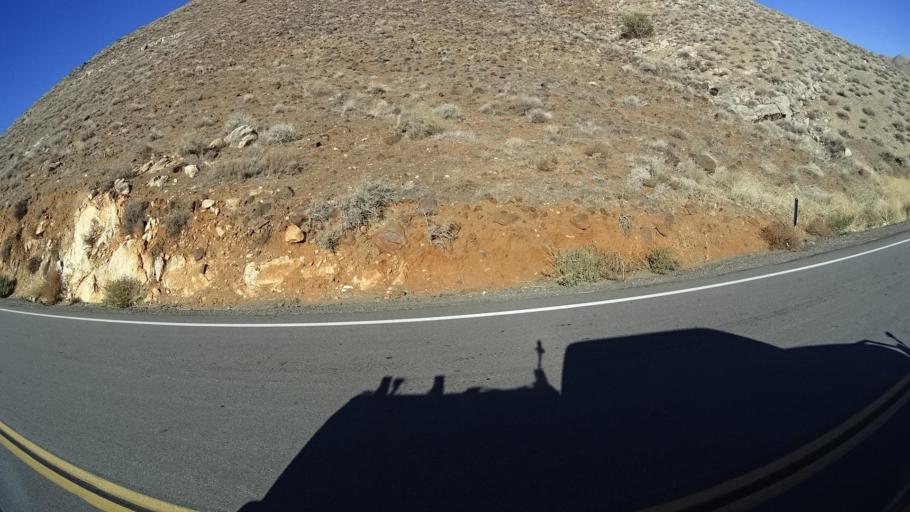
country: US
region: California
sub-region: Kern County
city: Wofford Heights
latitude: 35.6821
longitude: -118.3806
